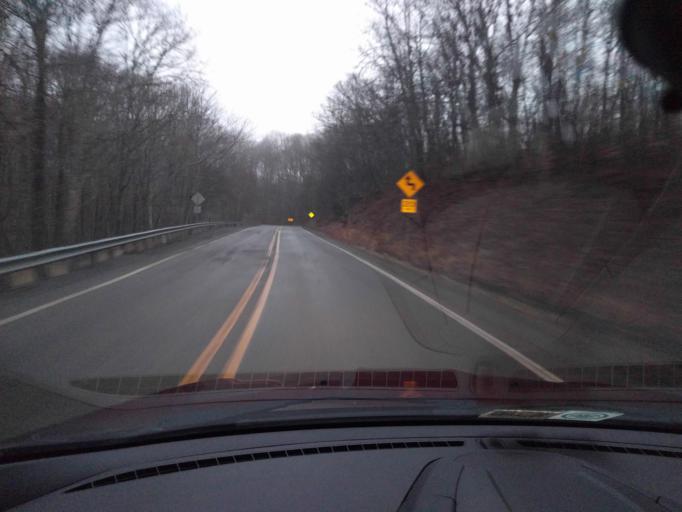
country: US
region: West Virginia
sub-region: Greenbrier County
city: Rainelle
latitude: 37.9841
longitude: -80.8399
